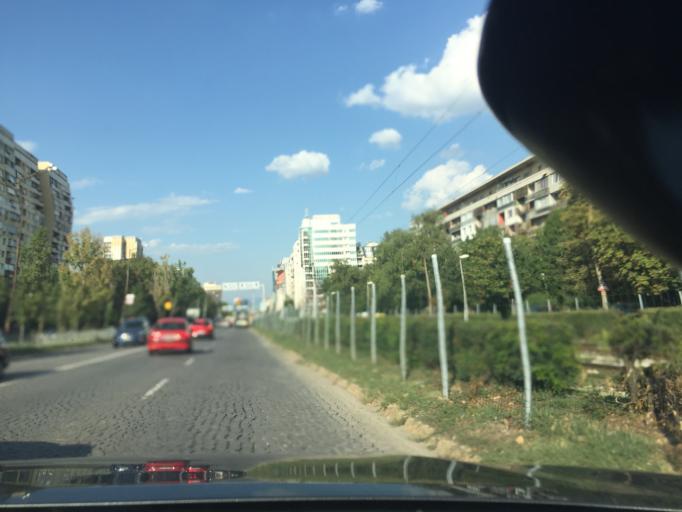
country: BG
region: Sofia-Capital
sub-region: Stolichna Obshtina
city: Sofia
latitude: 42.6841
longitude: 23.2948
